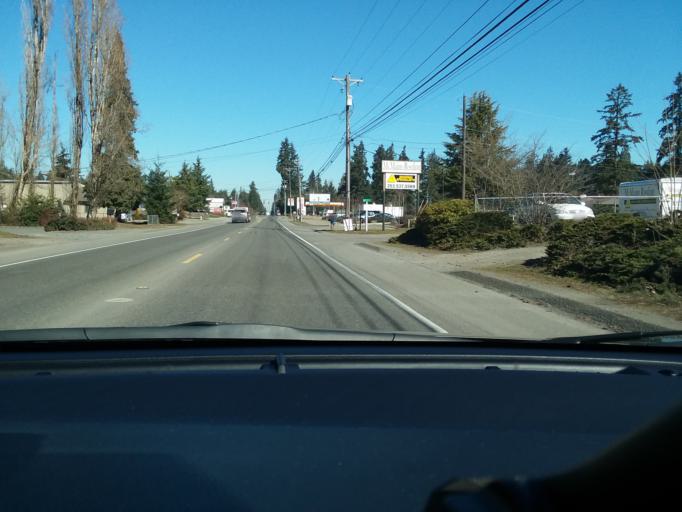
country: US
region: Washington
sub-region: Pierce County
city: Summit
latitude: 47.1787
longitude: -122.3571
